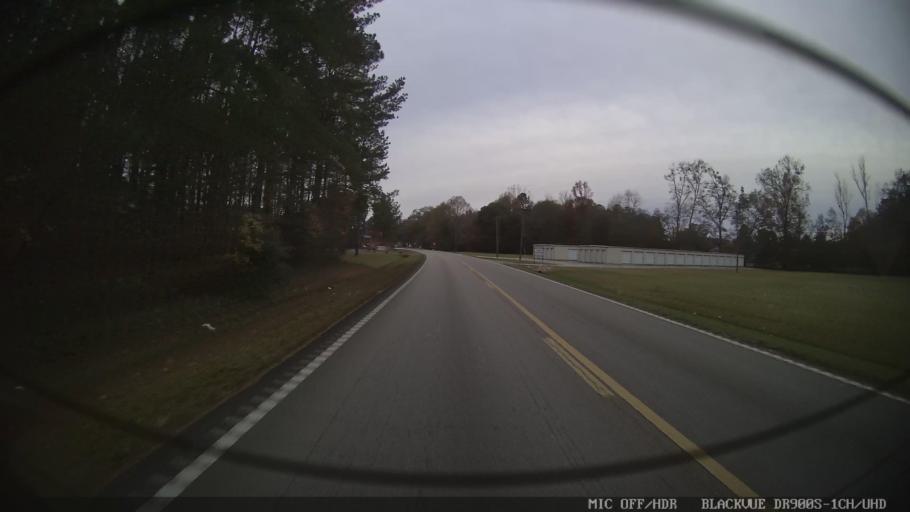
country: US
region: Mississippi
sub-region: Clarke County
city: Stonewall
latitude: 32.0384
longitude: -88.8792
